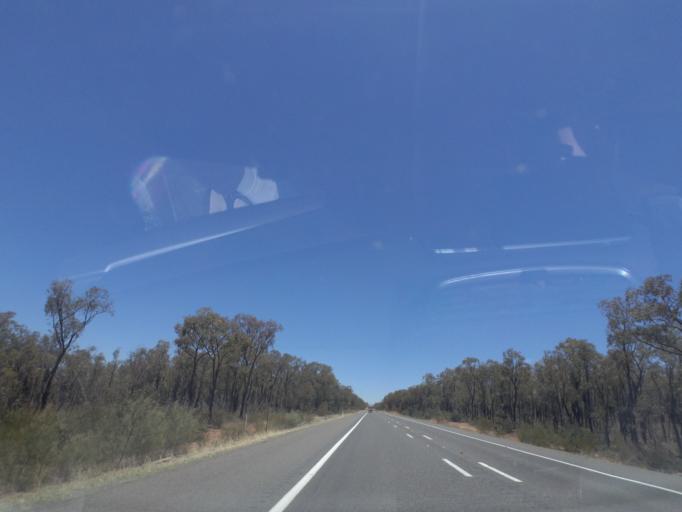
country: AU
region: New South Wales
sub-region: Warrumbungle Shire
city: Coonabarabran
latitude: -30.9073
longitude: 149.4372
